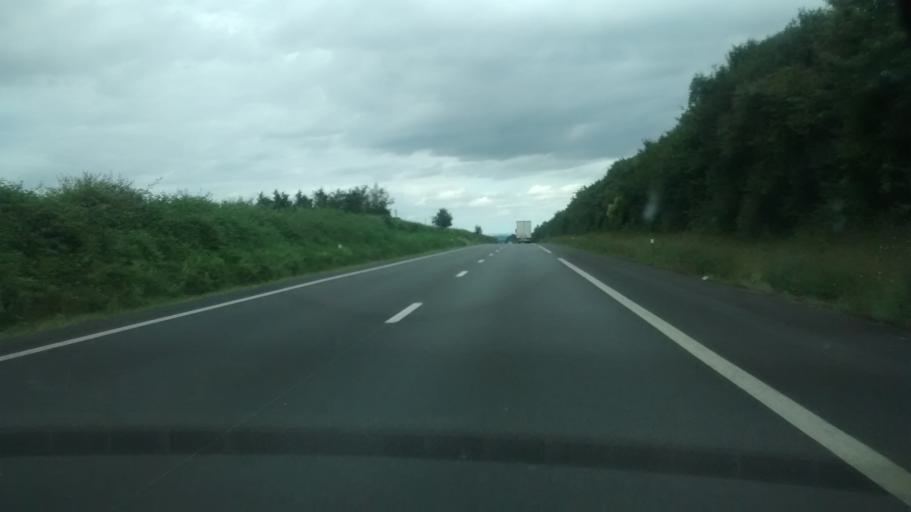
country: FR
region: Brittany
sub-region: Departement d'Ille-et-Vilaine
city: Monterfil
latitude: 48.0348
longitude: -1.9798
